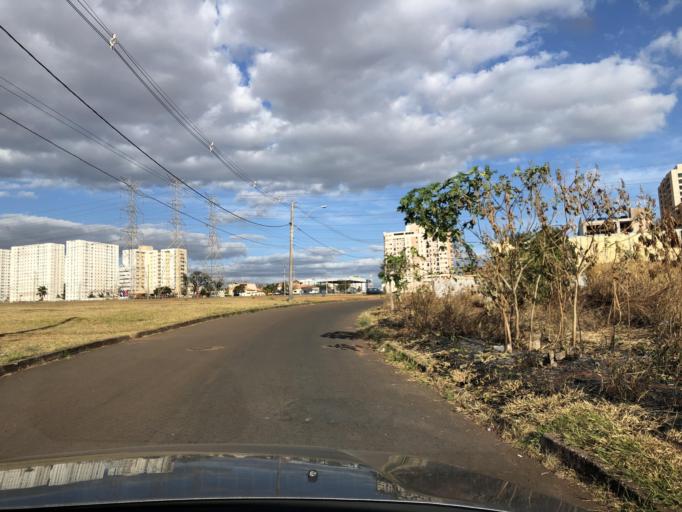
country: BR
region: Federal District
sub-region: Brasilia
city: Brasilia
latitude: -15.8743
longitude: -48.0919
